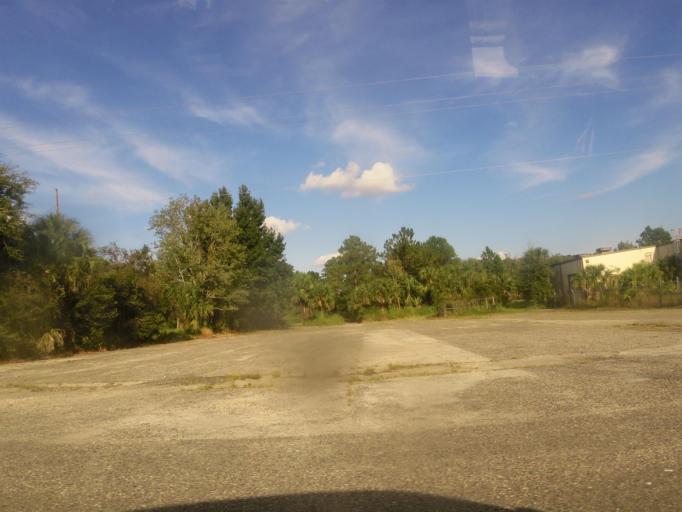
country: US
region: Florida
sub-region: Clay County
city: Green Cove Springs
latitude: 29.9829
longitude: -81.6714
